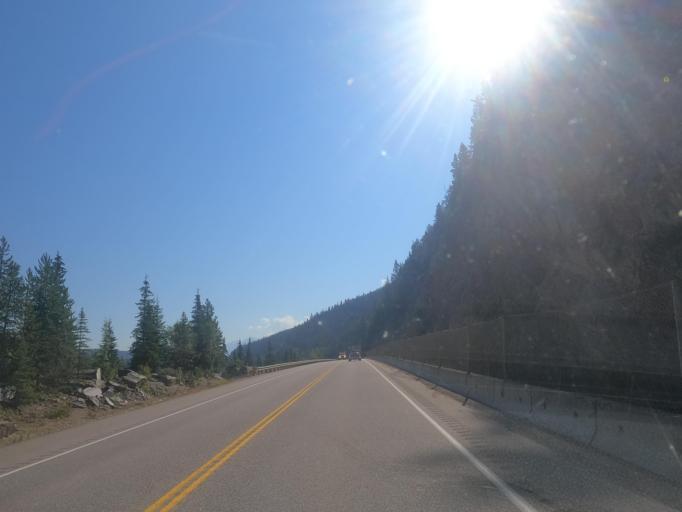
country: CA
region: Alberta
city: Jasper Park Lodge
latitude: 52.8738
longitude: -118.3066
